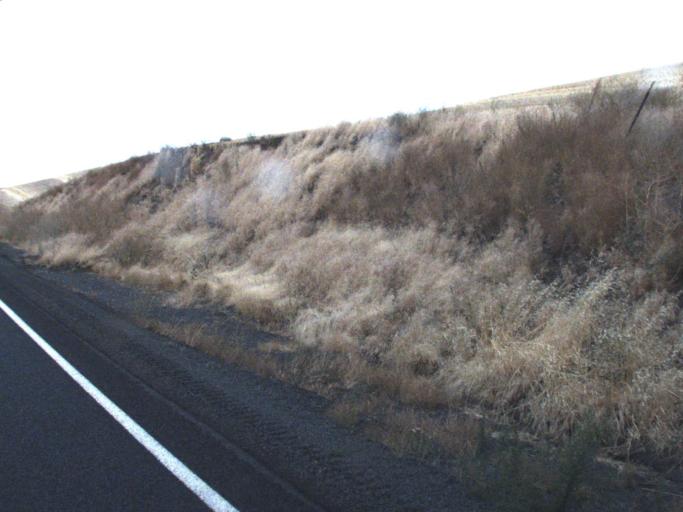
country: US
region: Washington
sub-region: Whitman County
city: Colfax
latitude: 47.1636
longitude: -117.2795
